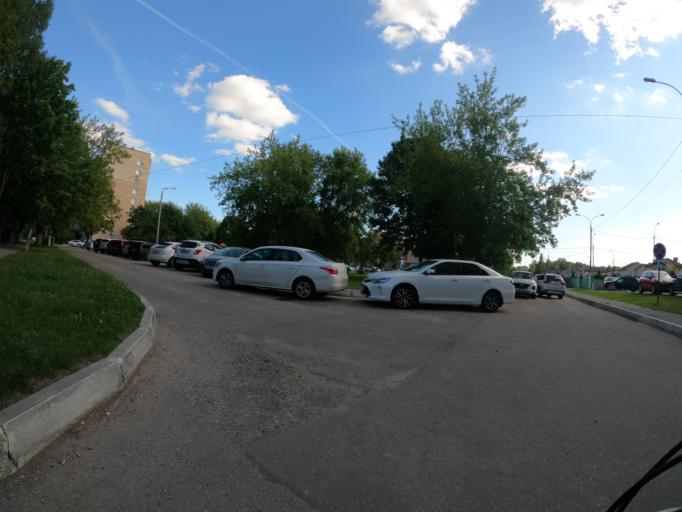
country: RU
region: Moskovskaya
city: Stupino
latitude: 54.8857
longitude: 38.0544
